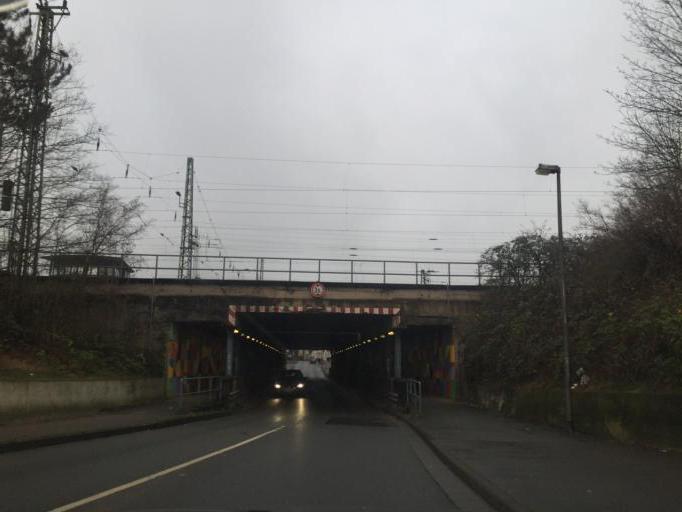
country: DE
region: Lower Saxony
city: Celle
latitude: 52.6177
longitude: 10.0628
